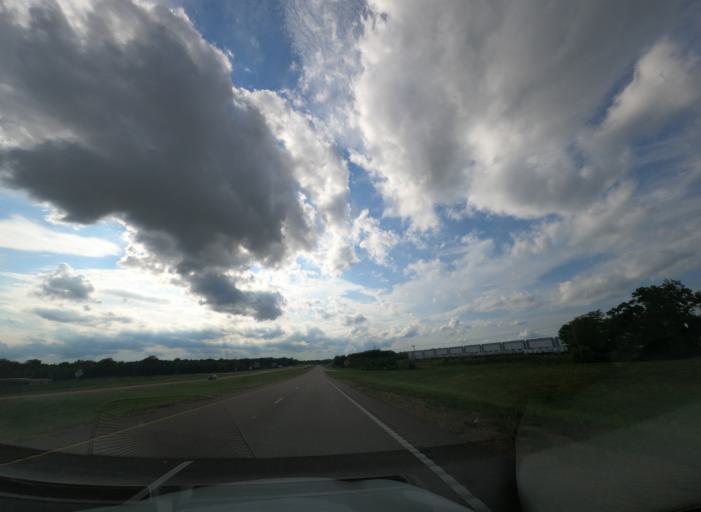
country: US
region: Tennessee
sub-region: Fayette County
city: Piperton
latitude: 34.9869
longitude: -89.5997
